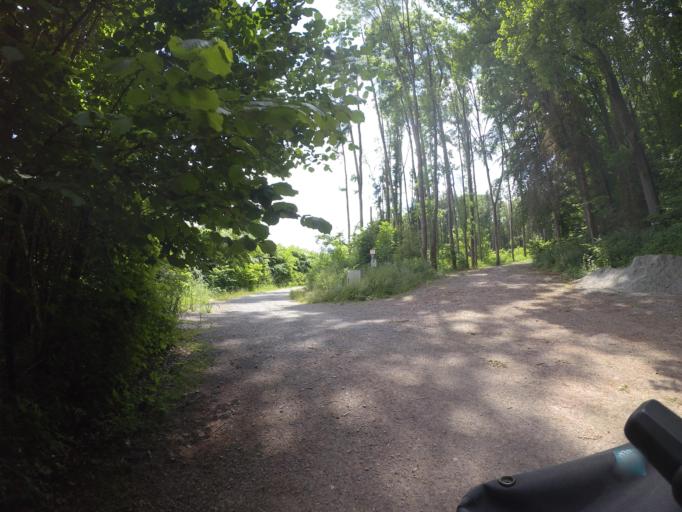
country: DE
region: Rheinland-Pfalz
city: Gries
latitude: 49.4135
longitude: 7.4042
